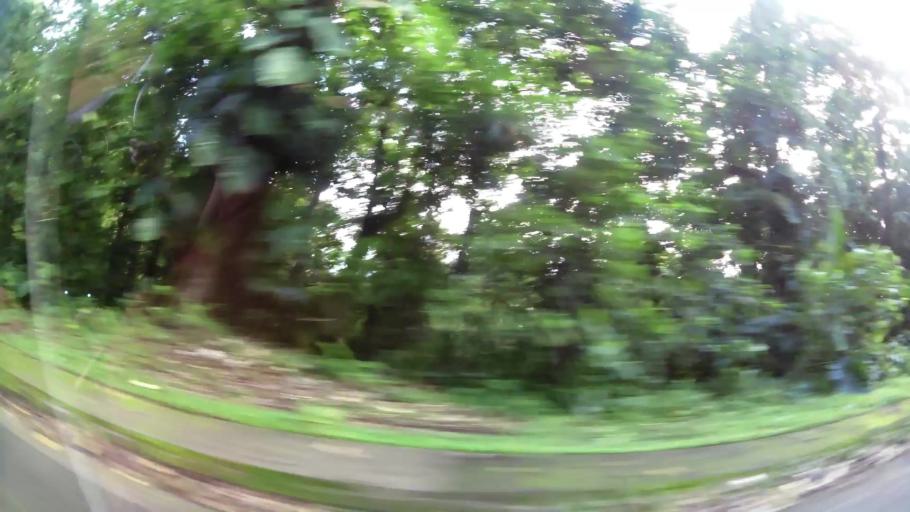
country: GP
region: Guadeloupe
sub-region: Guadeloupe
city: Bouillante
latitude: 16.1802
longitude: -61.7154
